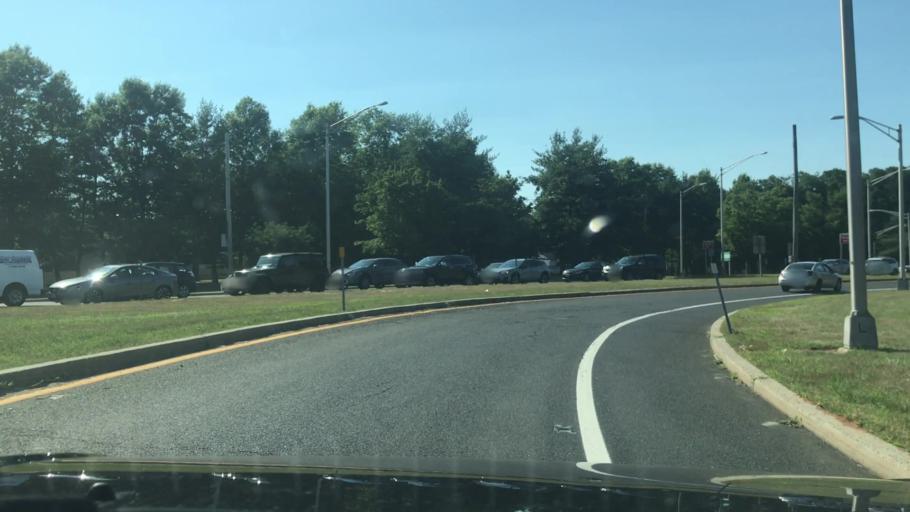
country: US
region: New Jersey
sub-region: Monmouth County
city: Lincroft
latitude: 40.3369
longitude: -74.1024
